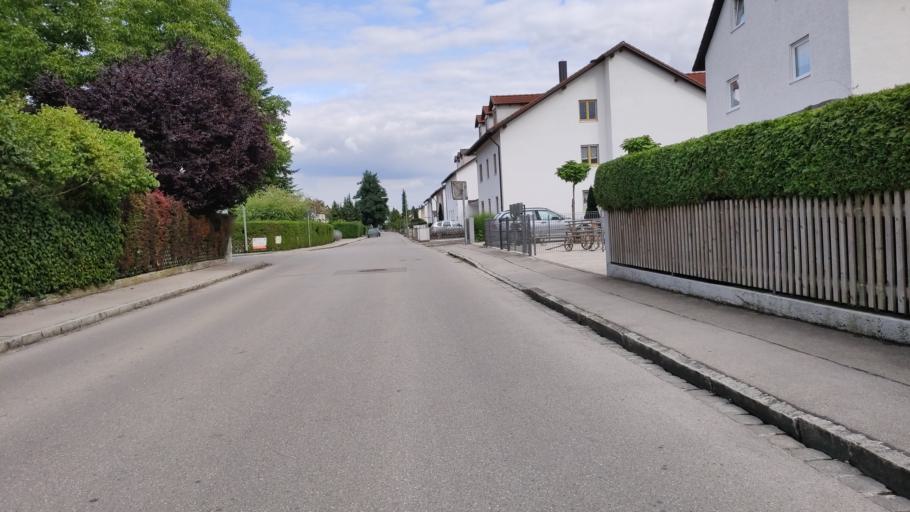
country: DE
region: Bavaria
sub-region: Swabia
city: Konigsbrunn
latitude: 48.2571
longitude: 10.8928
